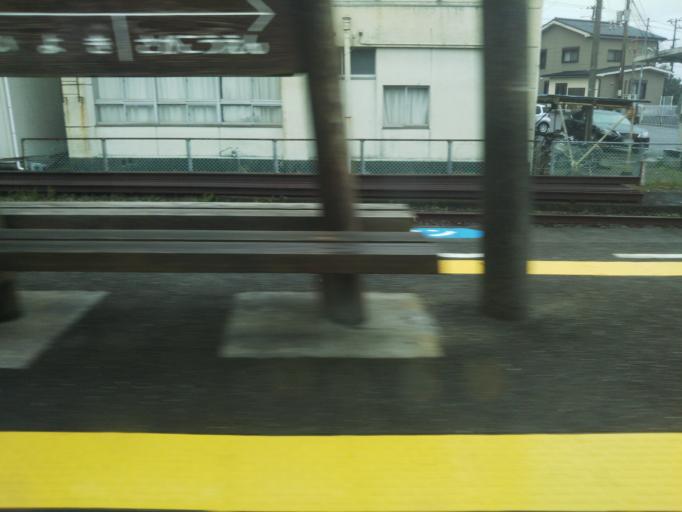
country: JP
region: Kochi
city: Nakamura
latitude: 33.0811
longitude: 133.1014
